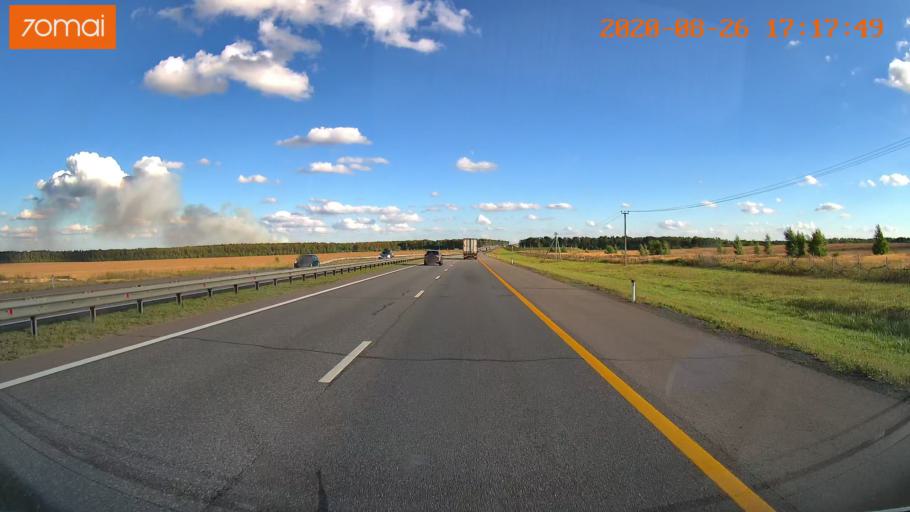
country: RU
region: Tula
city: Volovo
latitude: 53.6184
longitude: 38.0914
